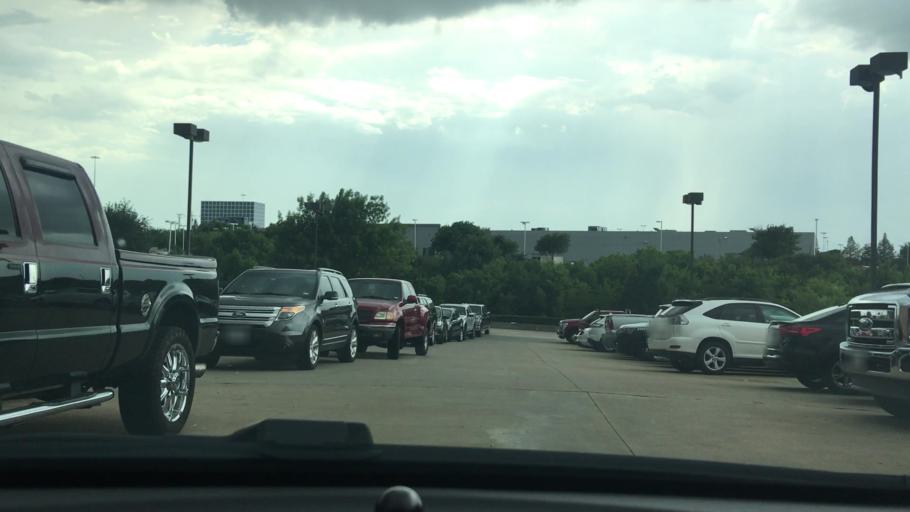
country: US
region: Texas
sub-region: Denton County
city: The Colony
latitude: 33.0914
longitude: -96.8277
